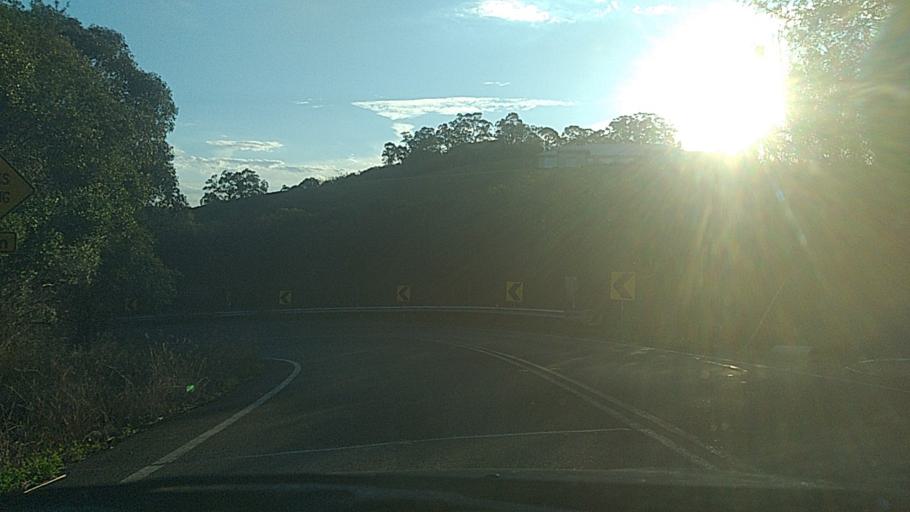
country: AU
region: New South Wales
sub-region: Wollondilly
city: Douglas Park
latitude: -34.1649
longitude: 150.7152
